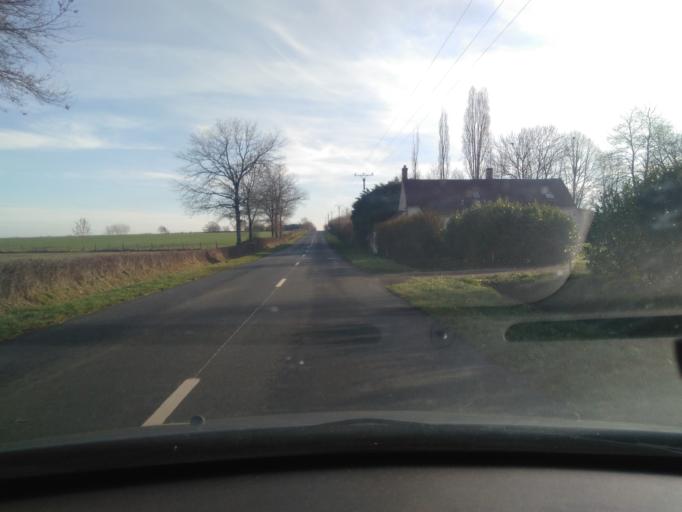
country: FR
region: Centre
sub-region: Departement du Cher
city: Chateaumeillant
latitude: 46.6357
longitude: 2.1197
